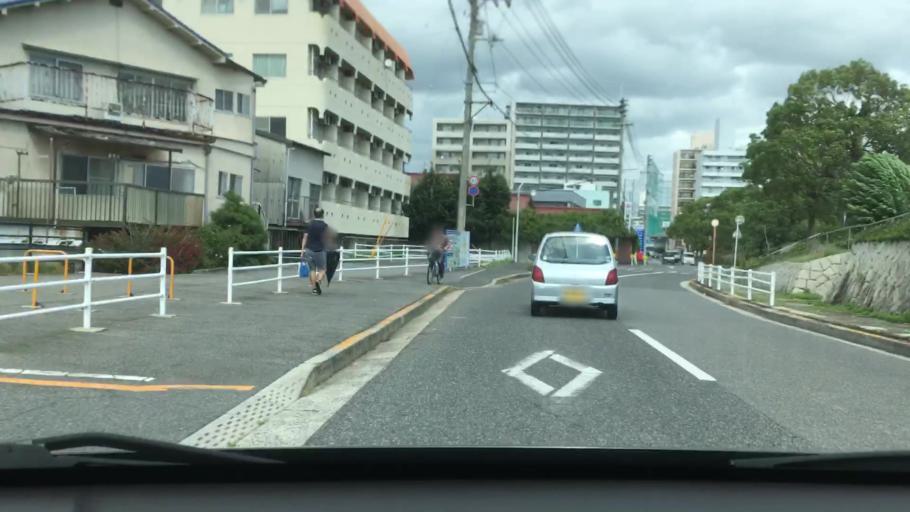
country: JP
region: Hiroshima
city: Hiroshima-shi
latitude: 34.3778
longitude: 132.4425
